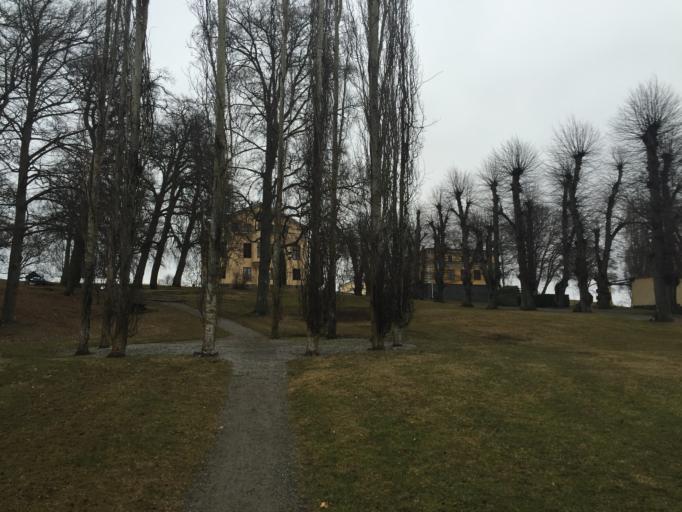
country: SE
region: Soedermanland
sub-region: Strangnas Kommun
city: Mariefred
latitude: 59.2464
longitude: 17.3080
